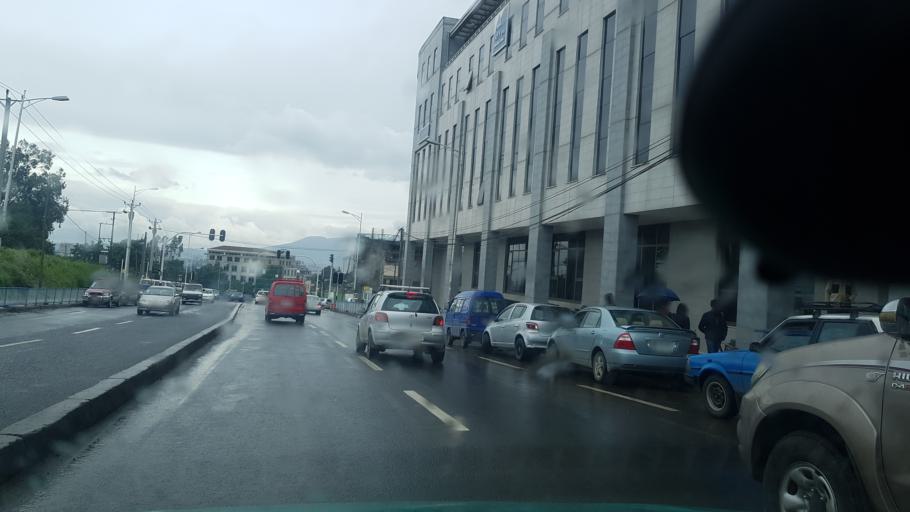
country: ET
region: Adis Abeba
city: Addis Ababa
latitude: 9.0298
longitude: 38.7620
